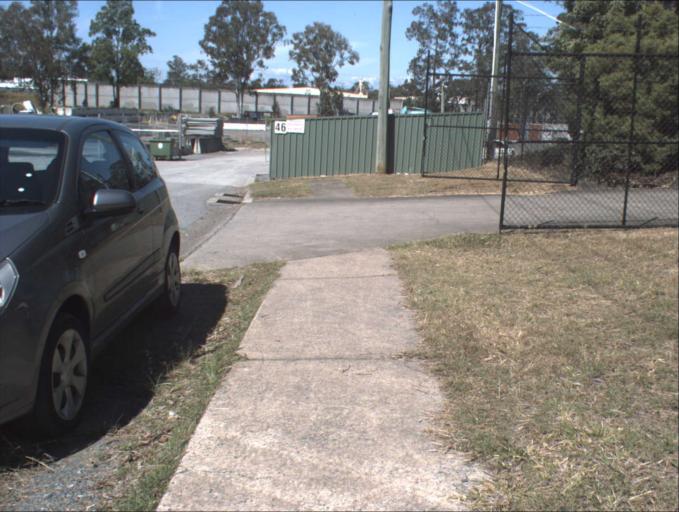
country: AU
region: Queensland
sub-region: Logan
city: Logan City
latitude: -27.6660
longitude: 153.1131
